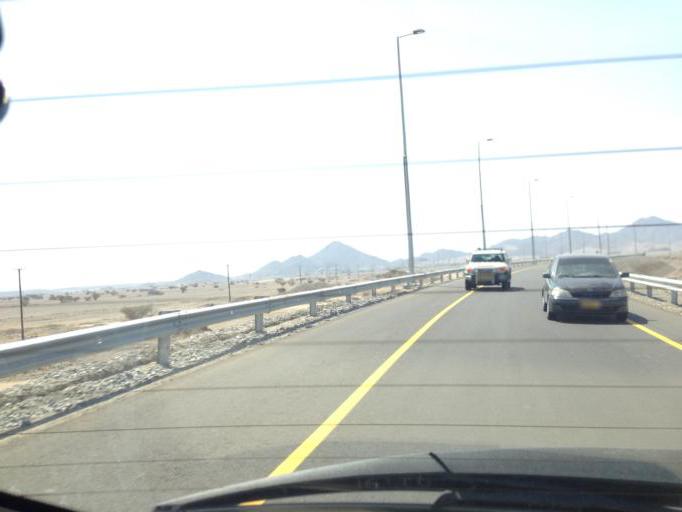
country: OM
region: Al Batinah
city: Rustaq
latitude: 23.5731
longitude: 57.4926
